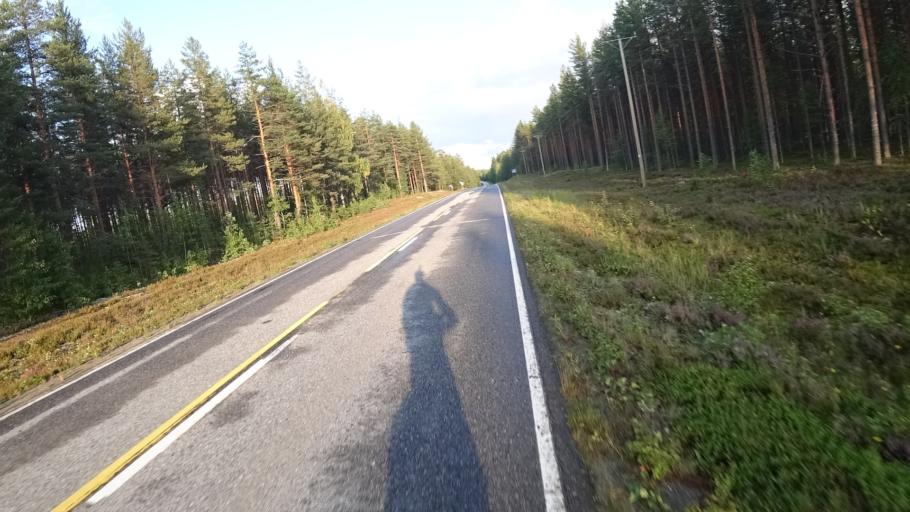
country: FI
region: North Karelia
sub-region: Joensuu
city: Ilomantsi
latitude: 62.6270
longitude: 31.1015
